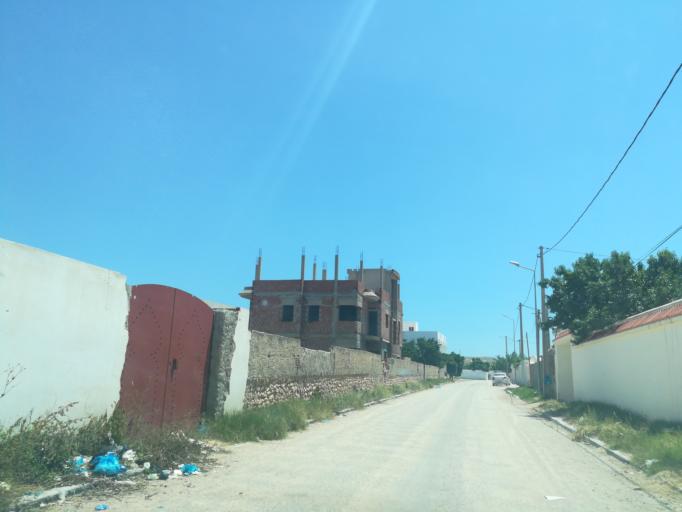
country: TN
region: Safaqis
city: Al Qarmadah
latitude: 34.8151
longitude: 10.7598
